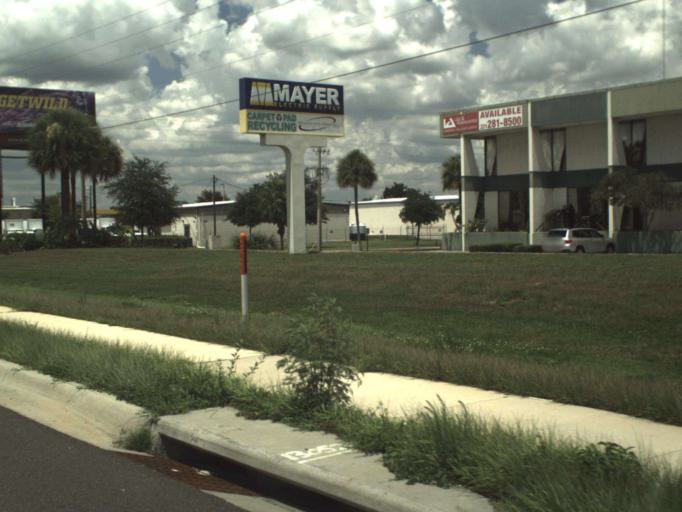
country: US
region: Florida
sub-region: Orange County
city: Fairview Shores
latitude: 28.5878
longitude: -81.4166
